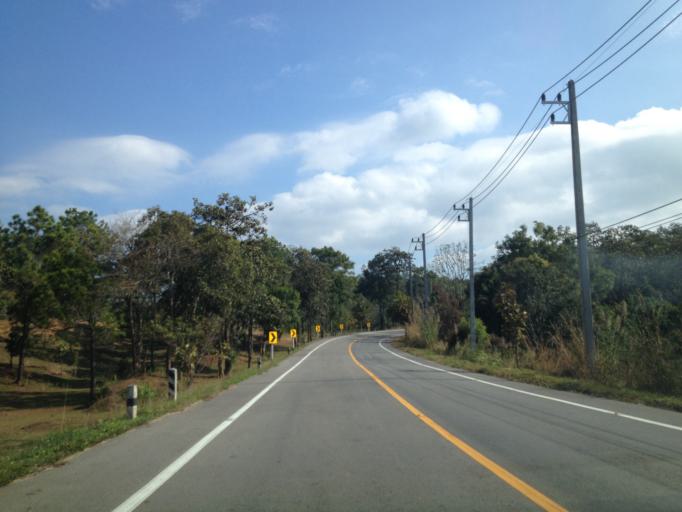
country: TH
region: Mae Hong Son
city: Pa Pae
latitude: 18.1601
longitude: 98.2796
